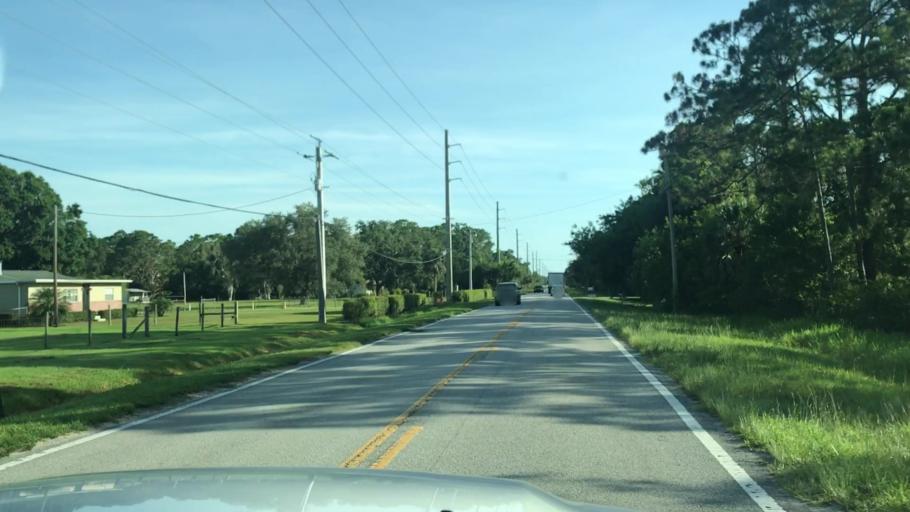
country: US
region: Florida
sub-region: Indian River County
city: Winter Beach
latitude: 27.7137
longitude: -80.4460
